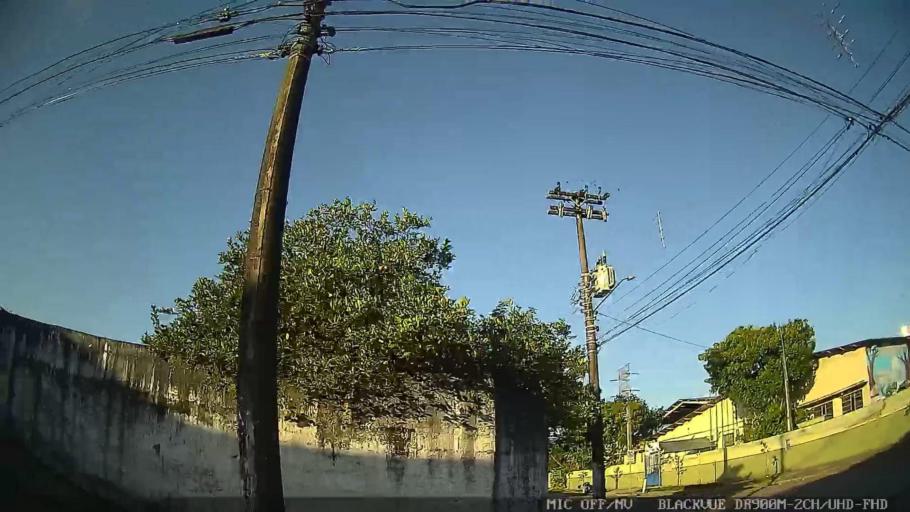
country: BR
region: Sao Paulo
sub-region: Guaruja
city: Guaruja
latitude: -23.9733
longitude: -46.2746
